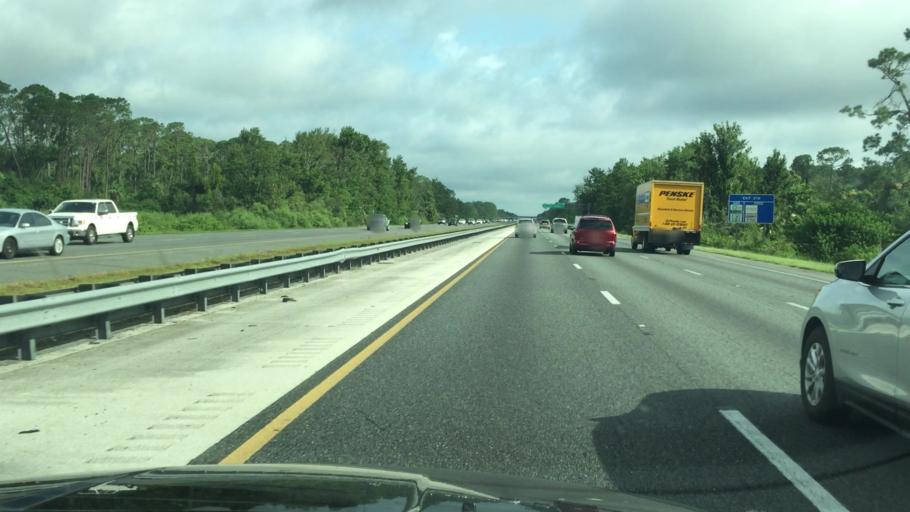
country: US
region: Florida
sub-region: Flagler County
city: Flagler Beach
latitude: 29.3927
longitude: -81.1503
